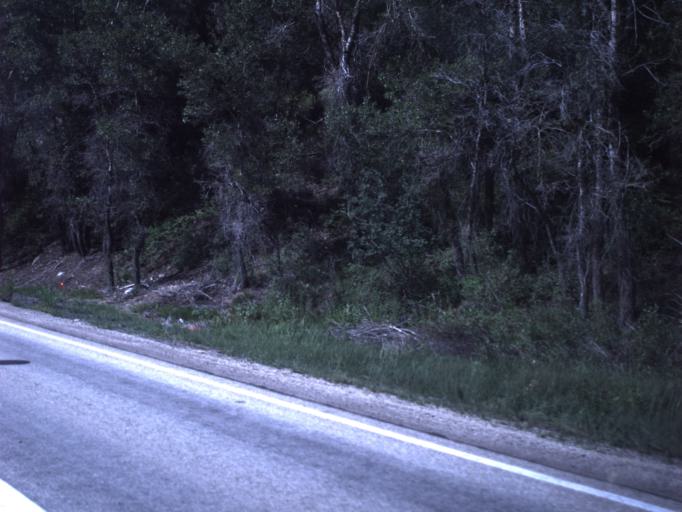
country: US
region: Utah
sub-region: Wasatch County
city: Heber
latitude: 40.3675
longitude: -111.2901
